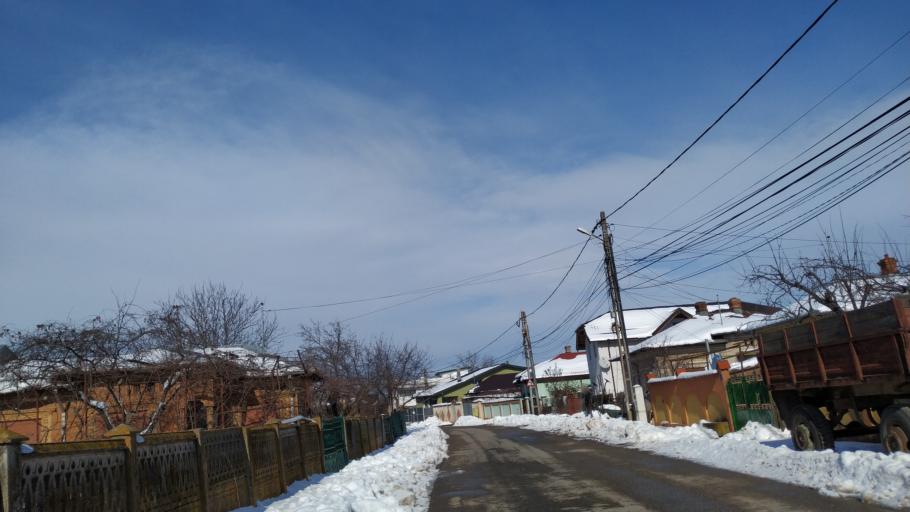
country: RO
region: Ilfov
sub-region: Comuna Berceni
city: Berceni
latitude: 44.3178
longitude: 26.1857
